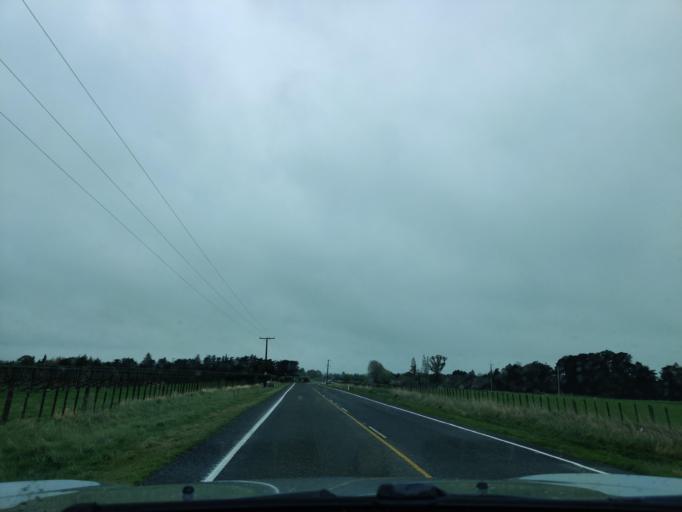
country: NZ
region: Hawke's Bay
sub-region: Hastings District
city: Hastings
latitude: -40.0208
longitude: 176.3168
